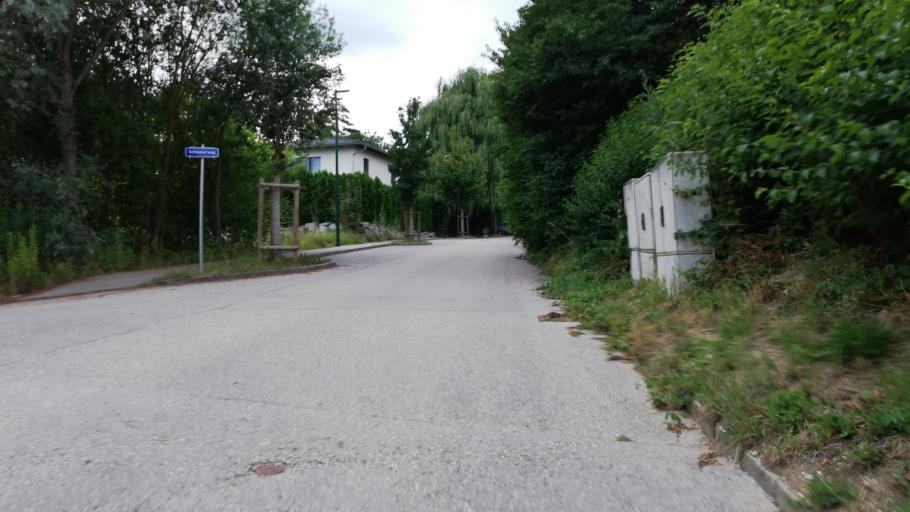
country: AT
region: Upper Austria
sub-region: Wels Stadt
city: Wels
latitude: 48.1878
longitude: 13.9982
